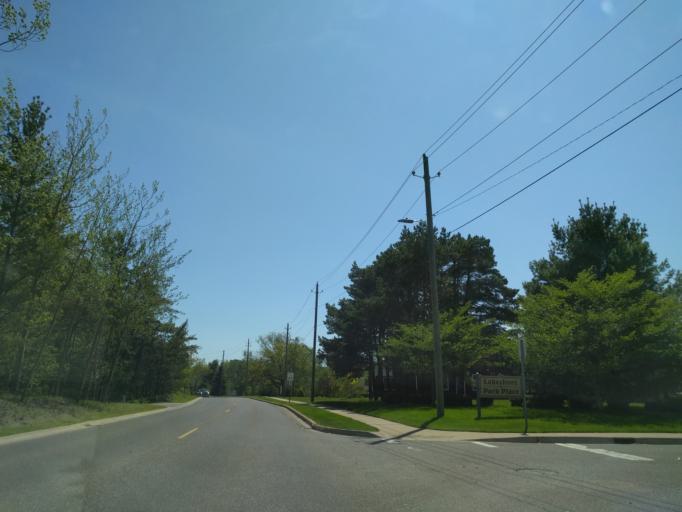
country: US
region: Michigan
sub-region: Marquette County
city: Marquette
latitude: 46.5548
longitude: -87.3836
